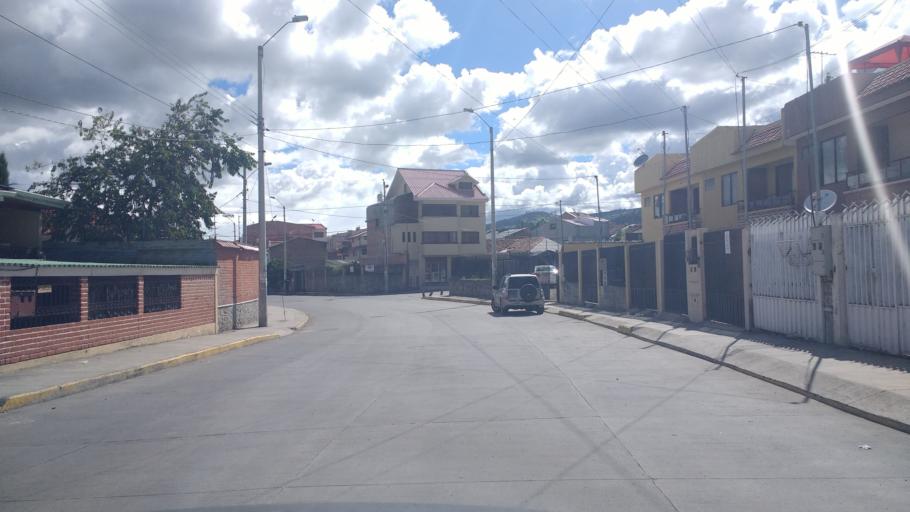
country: EC
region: Azuay
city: Cuenca
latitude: -2.8998
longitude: -79.0331
